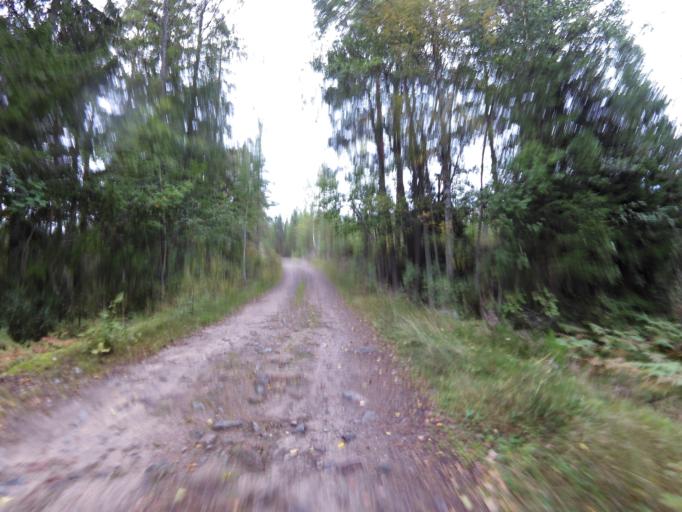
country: SE
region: Gaevleborg
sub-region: Gavle Kommun
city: Valbo
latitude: 60.7512
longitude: 16.9761
